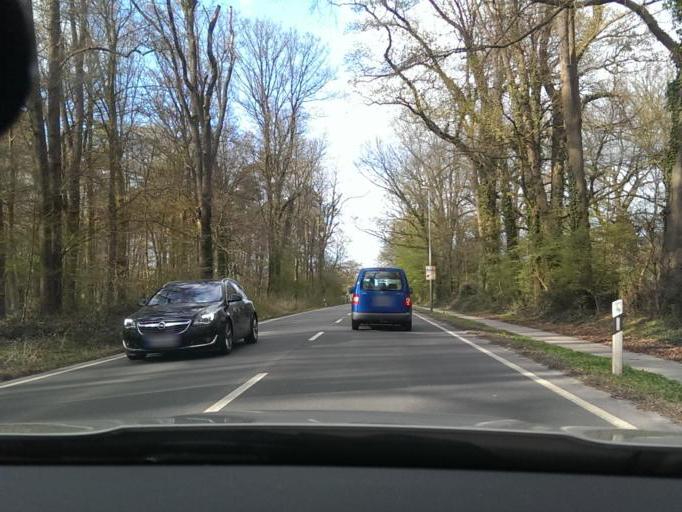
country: DE
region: Lower Saxony
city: Elze
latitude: 52.5231
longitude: 9.7251
